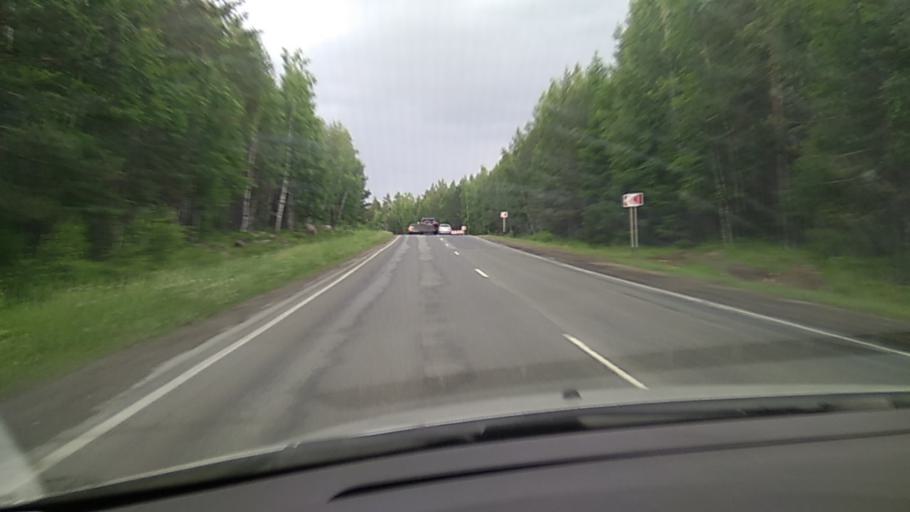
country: RU
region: Sverdlovsk
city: Neyvo-Rudyanka
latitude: 57.3820
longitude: 60.2227
